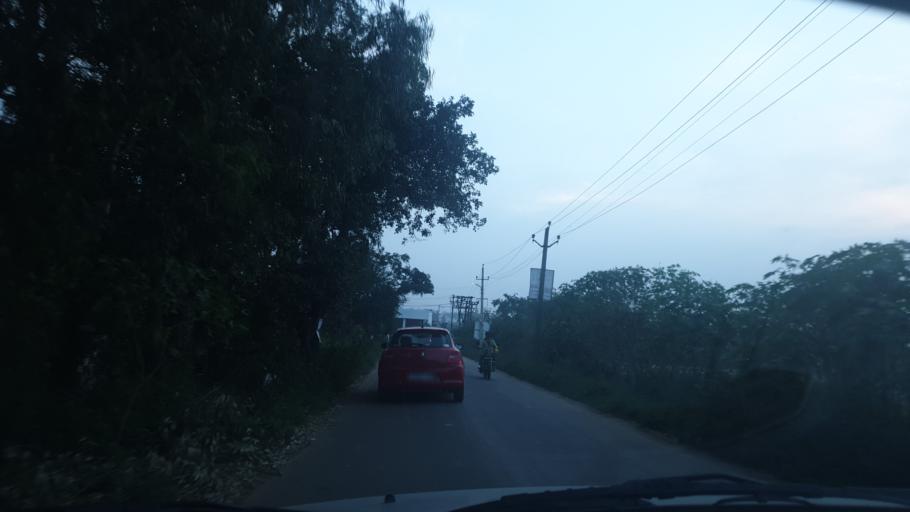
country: IN
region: Karnataka
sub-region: Bangalore Urban
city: Yelahanka
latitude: 13.0533
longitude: 77.6823
